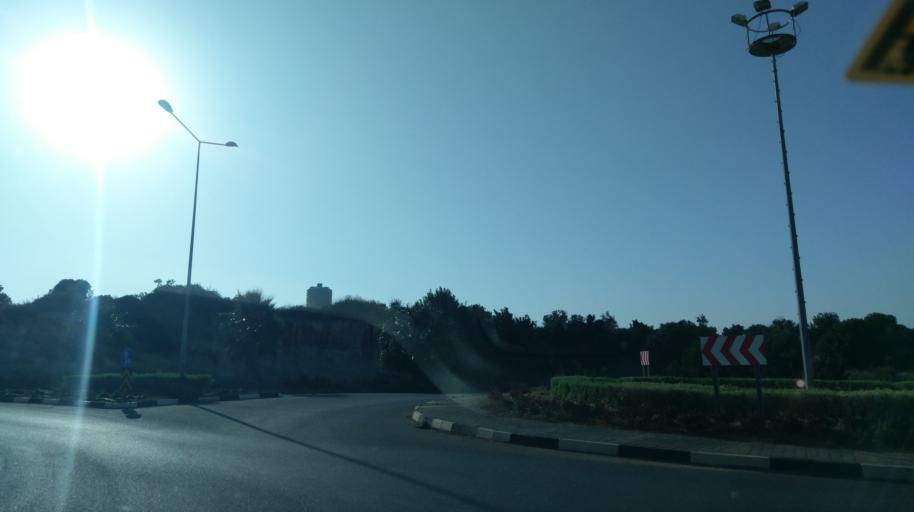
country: CY
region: Ammochostos
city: Leonarisso
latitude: 35.3807
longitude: 34.0682
